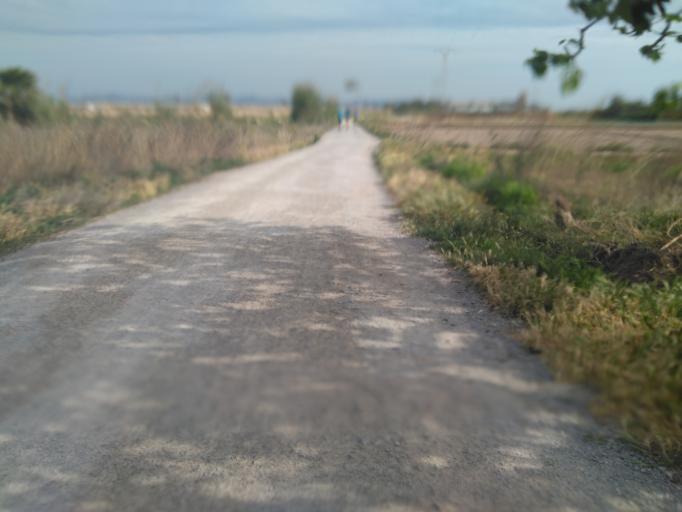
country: ES
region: Valencia
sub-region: Provincia de Valencia
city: Alboraya
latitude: 39.4960
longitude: -0.3256
